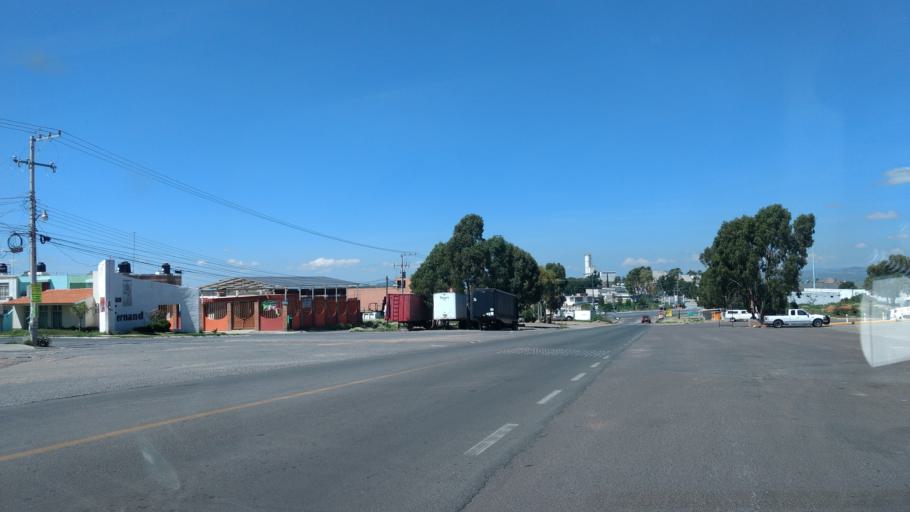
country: MX
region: Zacatecas
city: Zacatecas
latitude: 22.7702
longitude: -102.6114
